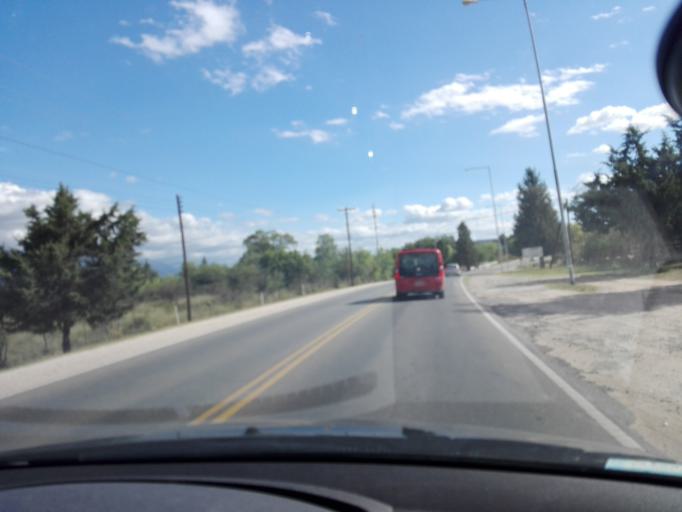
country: AR
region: Cordoba
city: Mina Clavero
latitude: -31.7893
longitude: -64.9983
